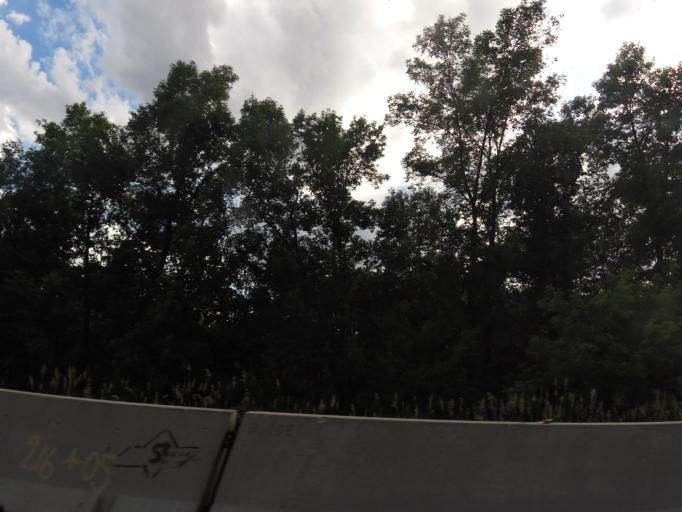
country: US
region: Minnesota
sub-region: Carver County
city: Chaska
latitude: 44.7803
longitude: -93.5976
